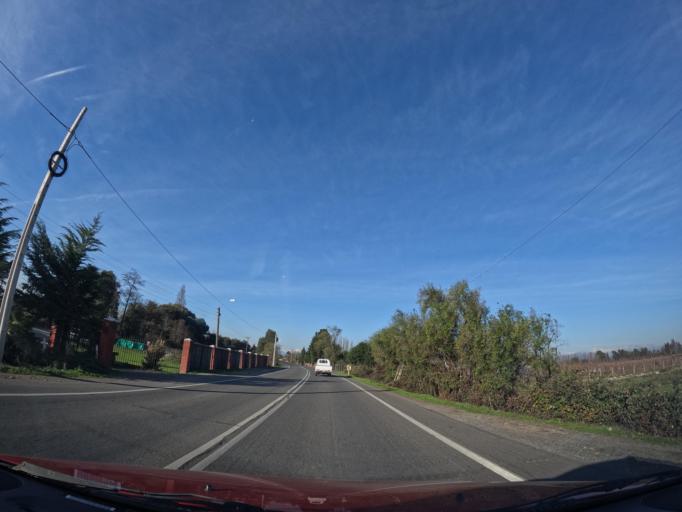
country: CL
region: Maule
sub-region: Provincia de Talca
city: San Clemente
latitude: -35.6232
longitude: -71.4996
